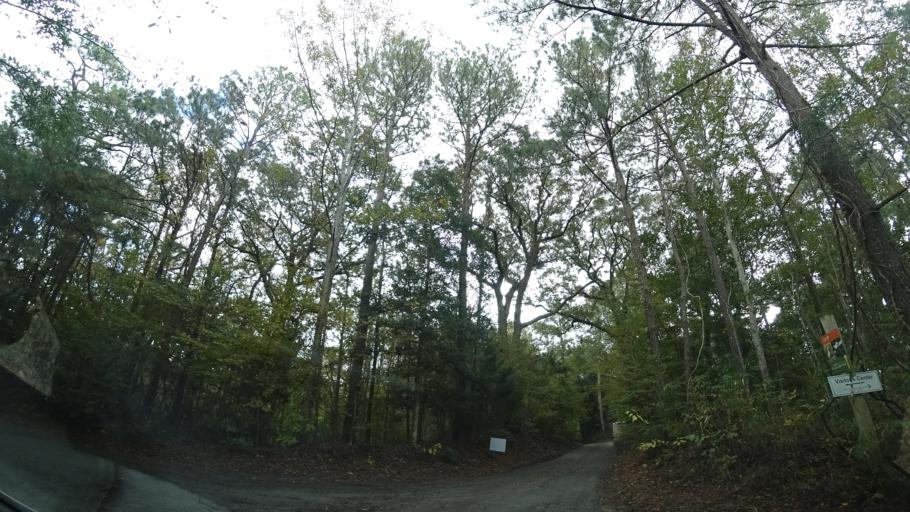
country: US
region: North Carolina
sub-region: Dare County
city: Kill Devil Hills
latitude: 35.9897
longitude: -75.6667
